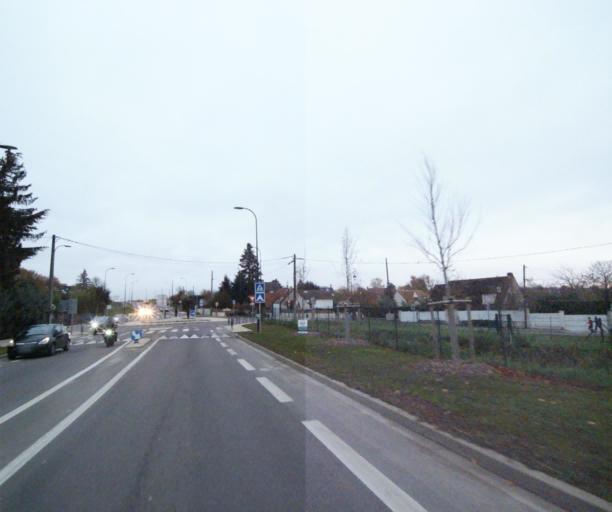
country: FR
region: Ile-de-France
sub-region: Departement des Yvelines
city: Villennes-sur-Seine
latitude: 48.9402
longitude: 1.9777
